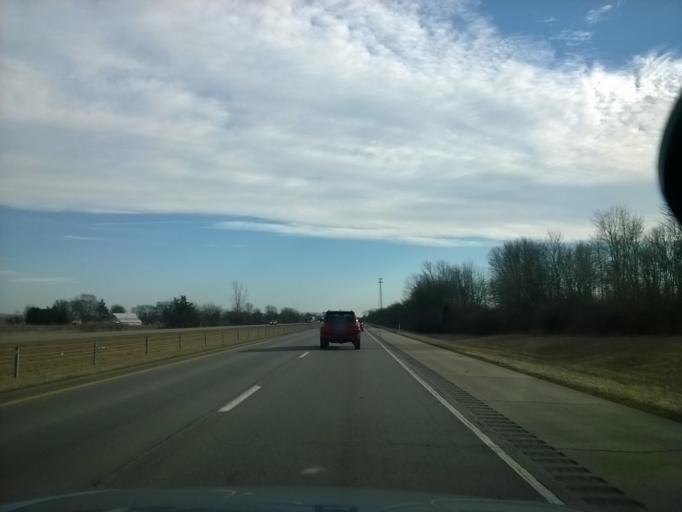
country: US
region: Indiana
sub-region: Johnson County
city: Edinburgh
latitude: 39.4294
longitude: -85.9759
